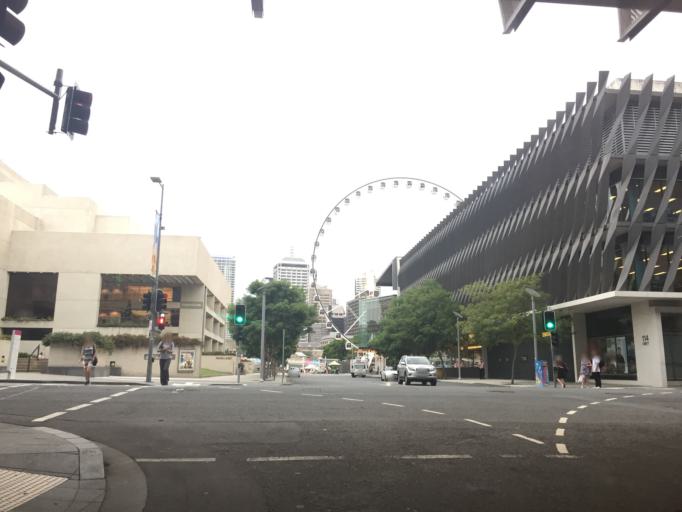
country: AU
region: Queensland
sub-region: Brisbane
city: South Brisbane
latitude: -27.4759
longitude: 153.0193
